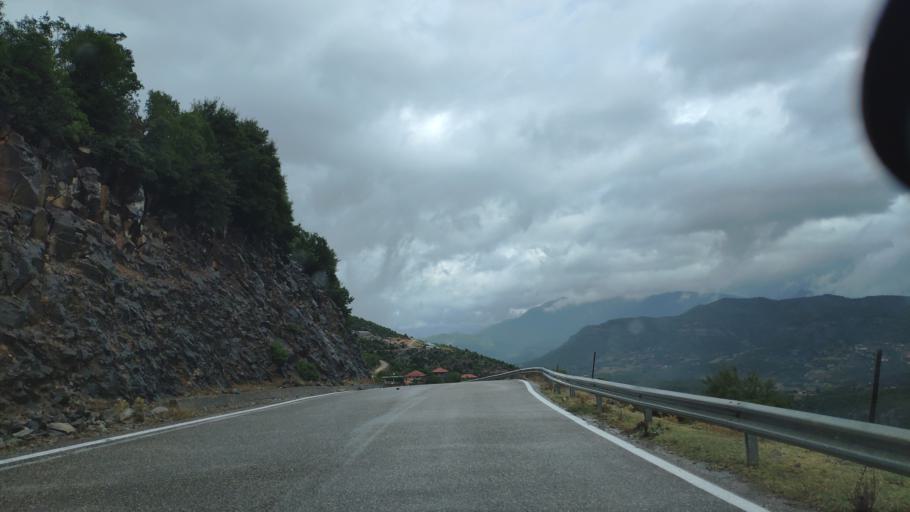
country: GR
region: Thessaly
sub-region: Nomos Kardhitsas
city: Anthiro
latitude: 39.1052
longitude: 21.4088
